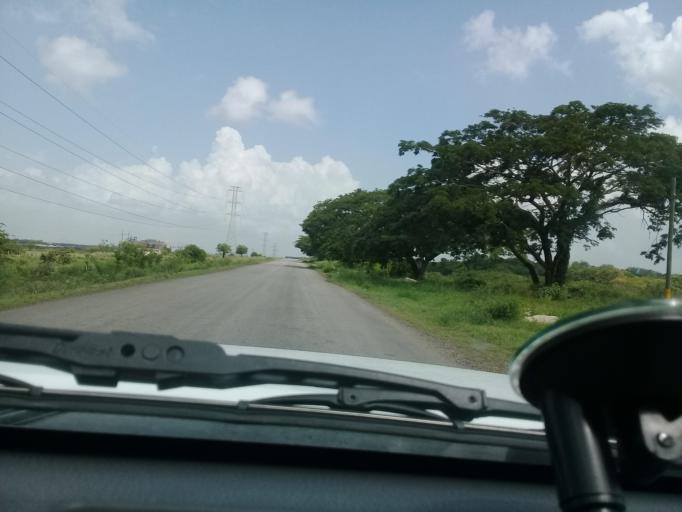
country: MX
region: Veracruz
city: Moralillo
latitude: 22.2263
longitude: -98.0124
